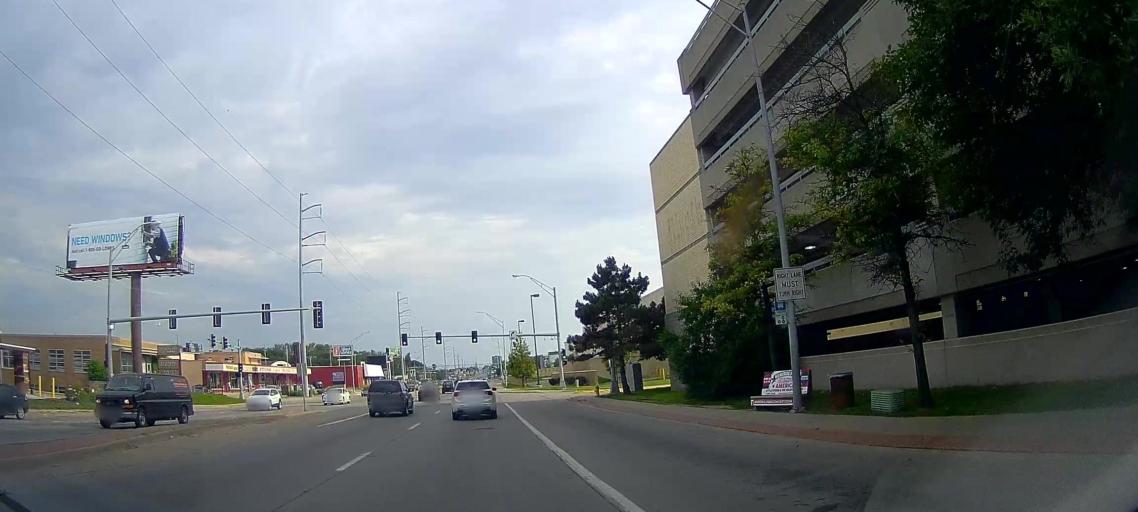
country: US
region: Nebraska
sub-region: Douglas County
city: Ralston
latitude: 41.2624
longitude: -96.0240
